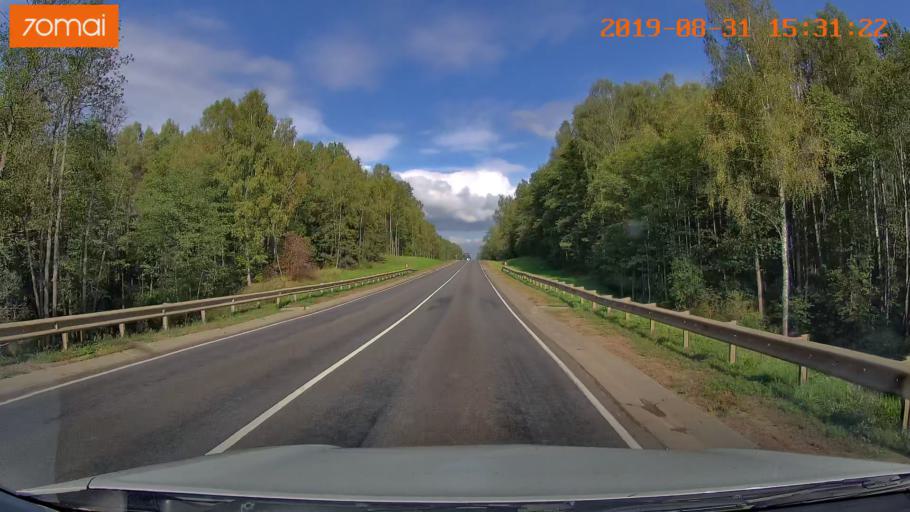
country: RU
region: Kaluga
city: Baryatino
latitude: 54.5820
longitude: 34.6530
